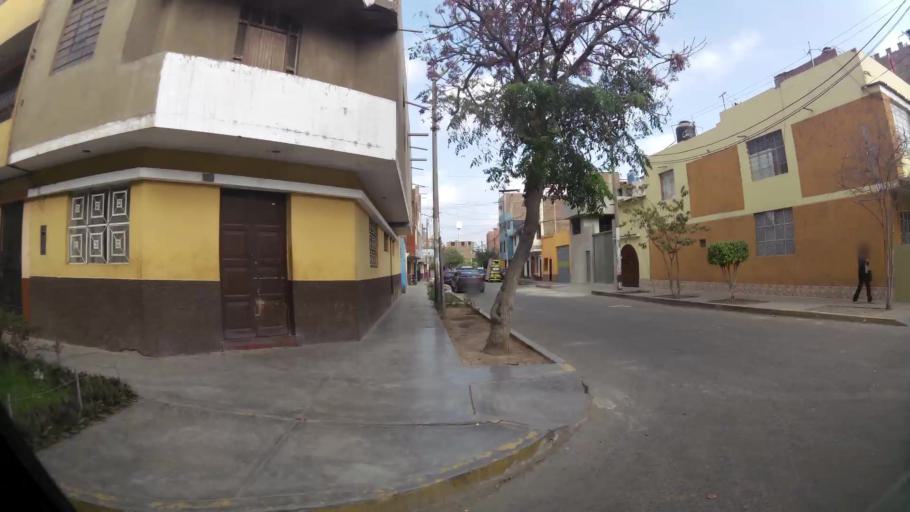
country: PE
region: La Libertad
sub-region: Provincia de Trujillo
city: El Porvenir
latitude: -8.1012
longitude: -79.0132
